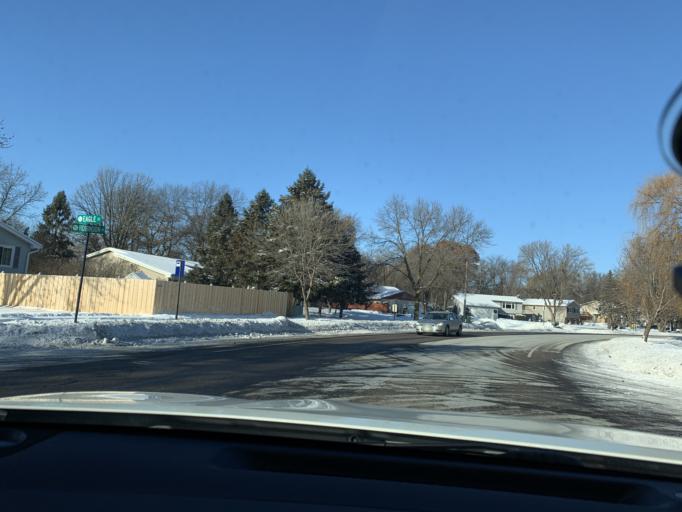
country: US
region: Minnesota
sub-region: Hennepin County
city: West Coon Rapids
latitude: 45.1676
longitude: -93.3036
